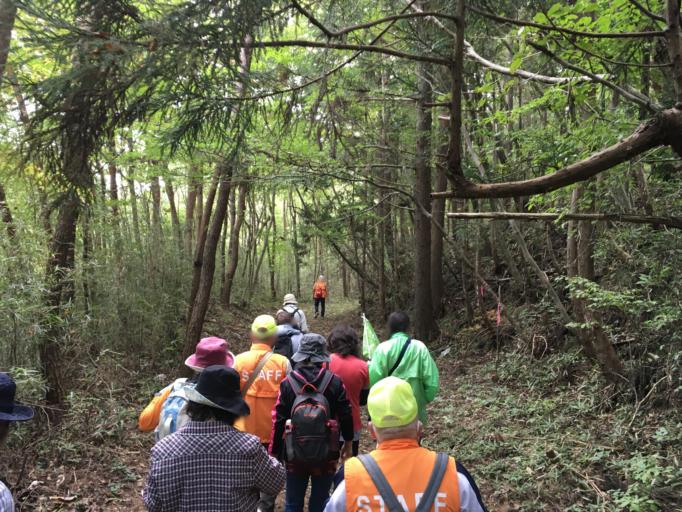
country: JP
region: Iwate
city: Ichinoseki
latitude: 38.8837
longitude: 141.0845
